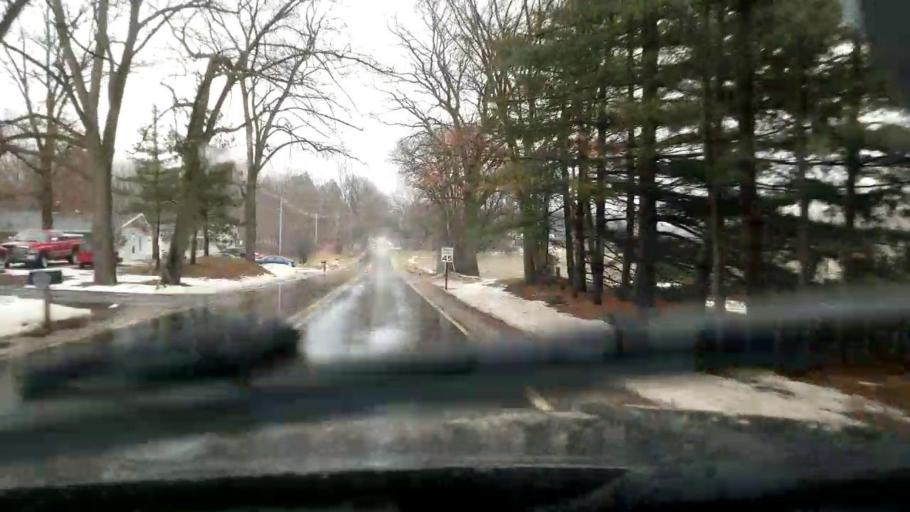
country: US
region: Michigan
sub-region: Jackson County
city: Michigan Center
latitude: 42.2841
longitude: -84.3525
